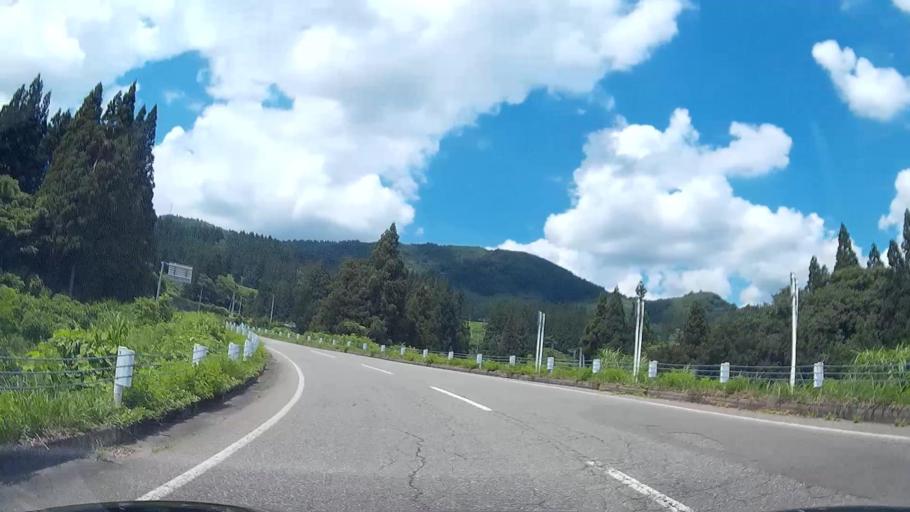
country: JP
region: Niigata
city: Shiozawa
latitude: 37.0221
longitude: 138.8058
